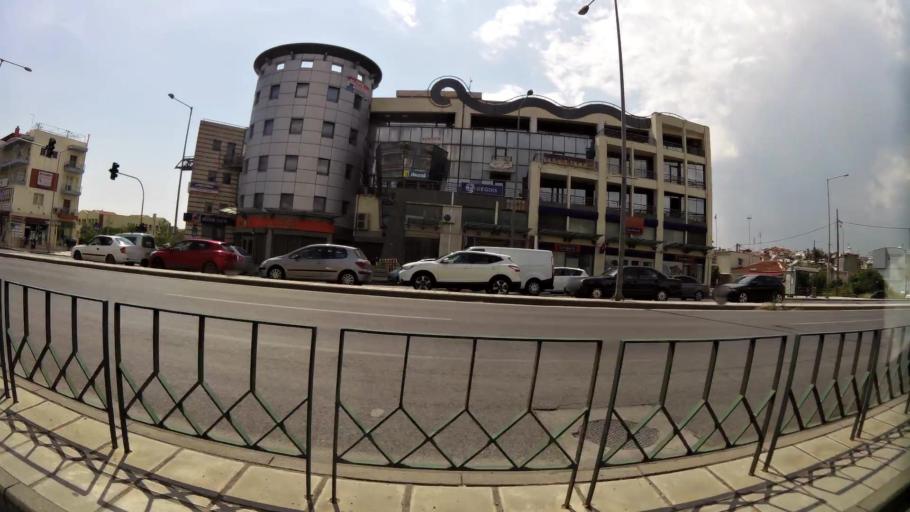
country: GR
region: Central Macedonia
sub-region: Nomos Thessalonikis
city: Stavroupoli
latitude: 40.6719
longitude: 22.9391
